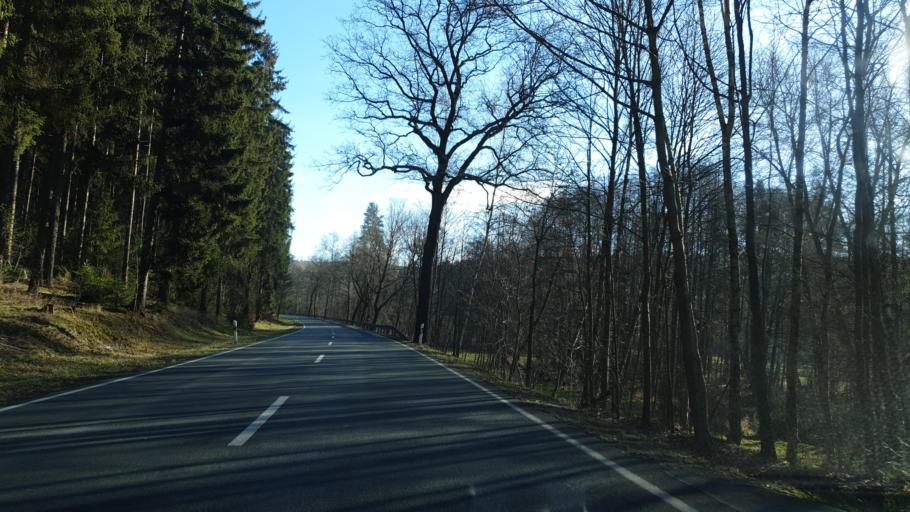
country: DE
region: Saxony
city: Adorf
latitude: 50.2787
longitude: 12.2855
